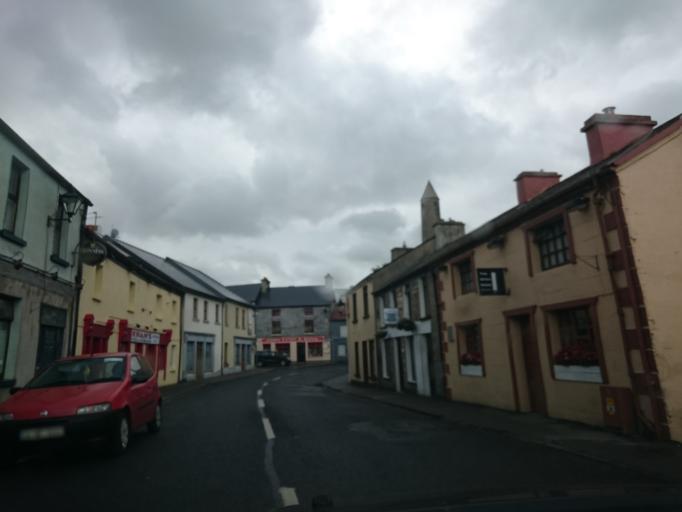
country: IE
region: Connaught
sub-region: Maigh Eo
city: Ballina
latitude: 54.2137
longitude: -9.2220
